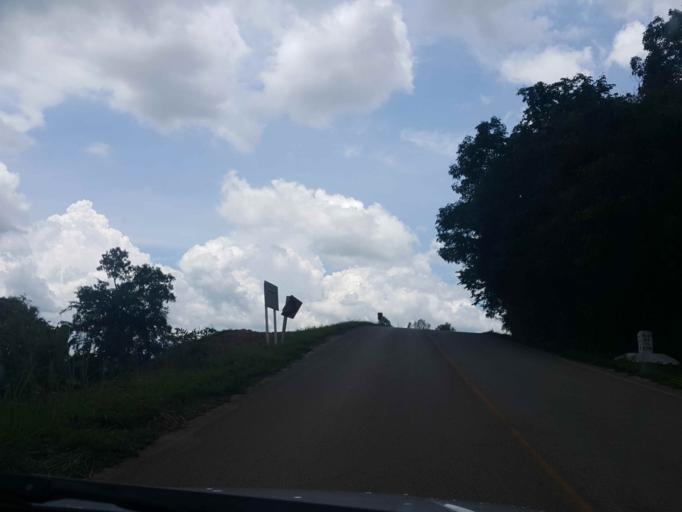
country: TH
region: Lampang
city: Ngao
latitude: 18.9460
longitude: 100.0782
